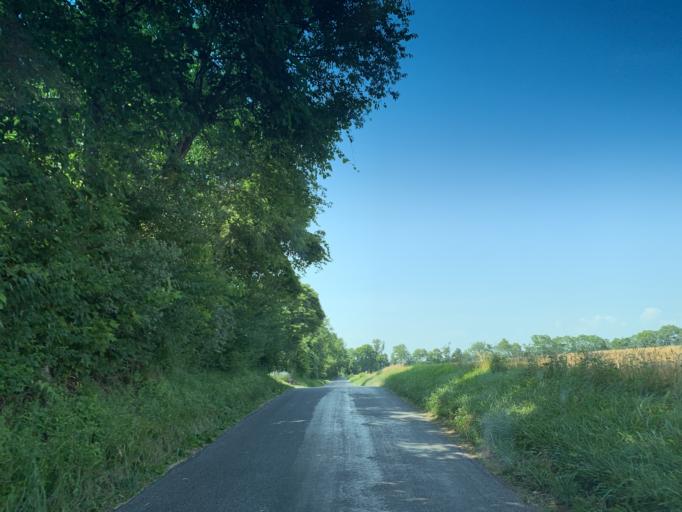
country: US
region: Maryland
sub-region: Montgomery County
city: Poolesville
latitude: 39.1405
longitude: -77.4513
